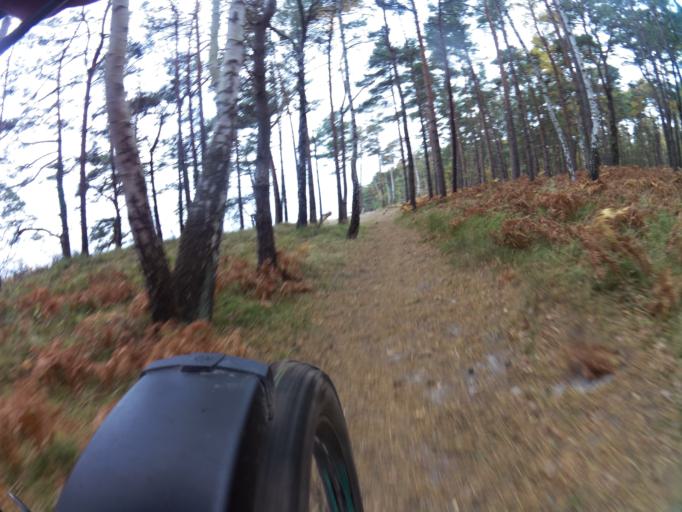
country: PL
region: Pomeranian Voivodeship
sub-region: Powiat pucki
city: Jastarnia
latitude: 54.6871
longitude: 18.7033
